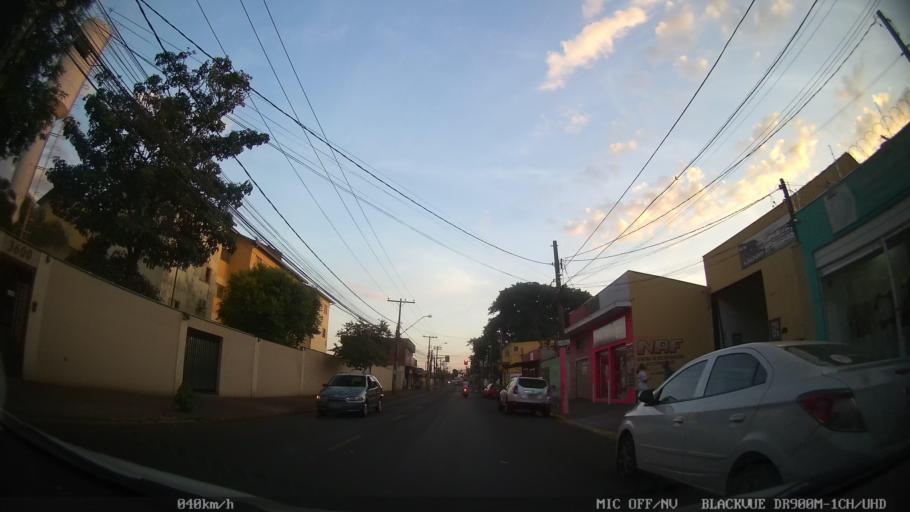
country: BR
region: Sao Paulo
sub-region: Ribeirao Preto
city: Ribeirao Preto
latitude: -21.1330
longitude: -47.8157
